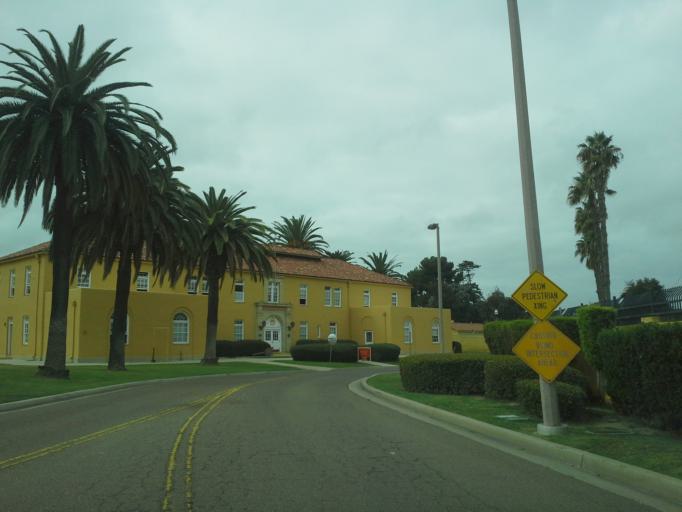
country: US
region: California
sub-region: San Diego County
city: San Diego
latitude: 32.7453
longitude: -117.1967
